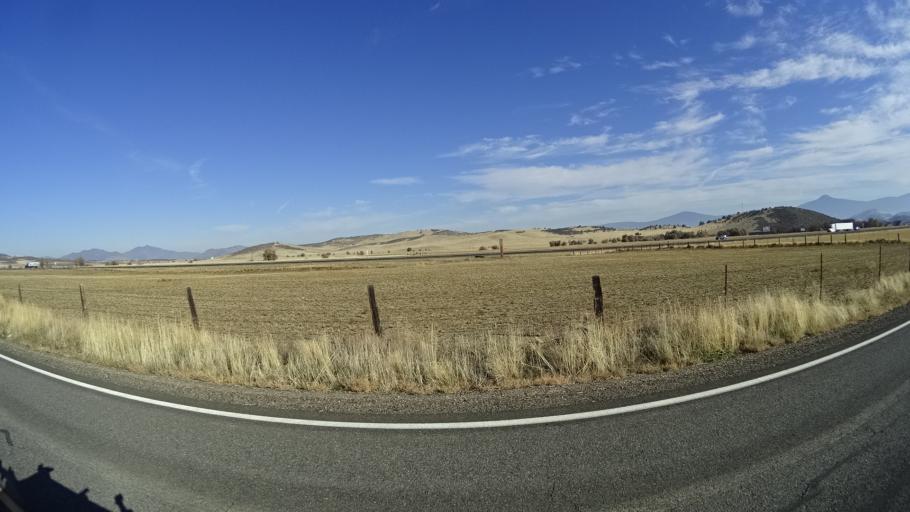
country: US
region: California
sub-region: Siskiyou County
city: Montague
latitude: 41.6483
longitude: -122.5465
